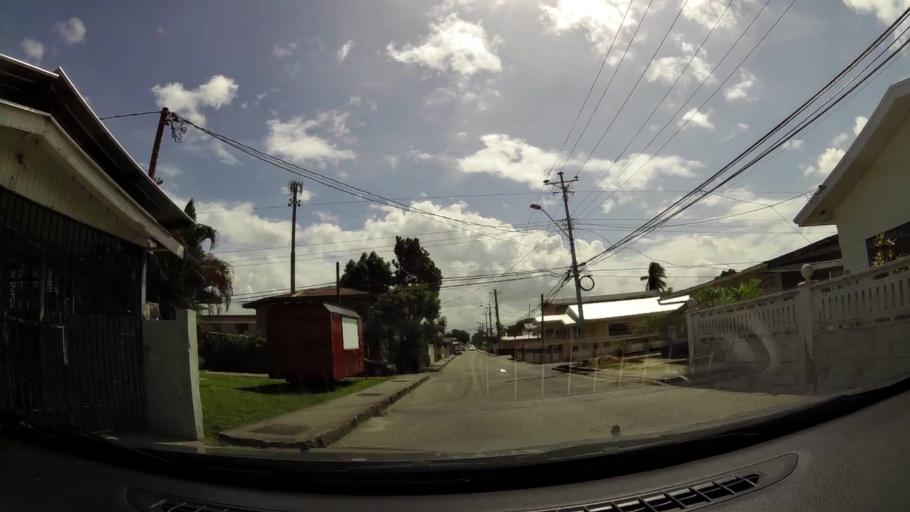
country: TT
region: Borough of Arima
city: Arima
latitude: 10.6295
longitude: -61.2815
